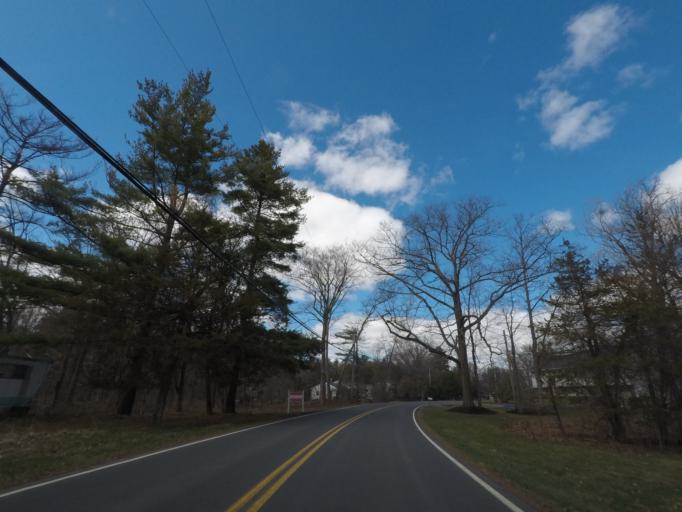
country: US
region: New York
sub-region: Albany County
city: Delmar
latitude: 42.5765
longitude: -73.8300
